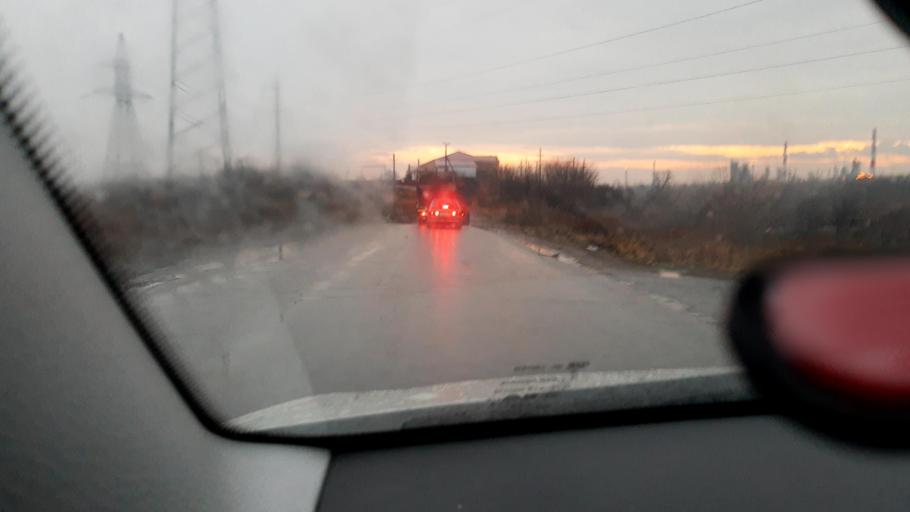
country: RU
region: Bashkortostan
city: Ufa
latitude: 54.8658
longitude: 56.1283
